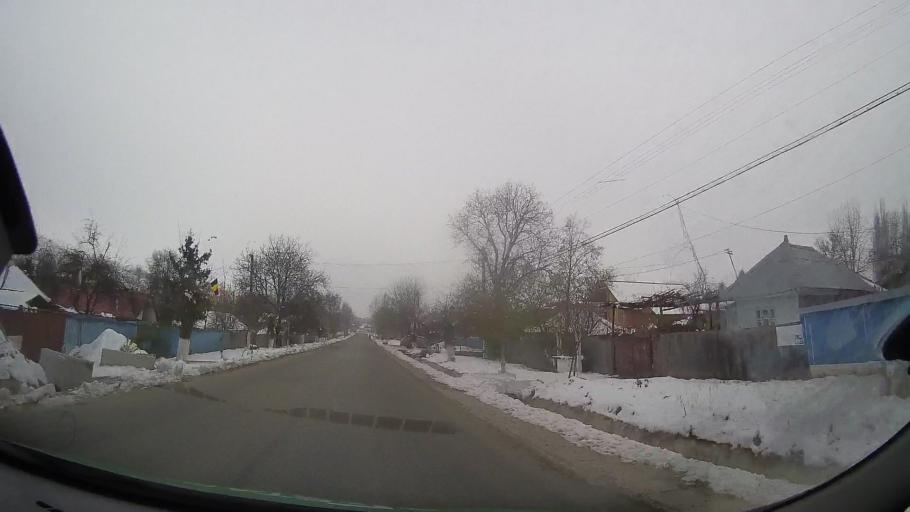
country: RO
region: Bacau
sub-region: Comuna Glavanesti
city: Frumuselu
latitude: 46.2959
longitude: 27.3004
